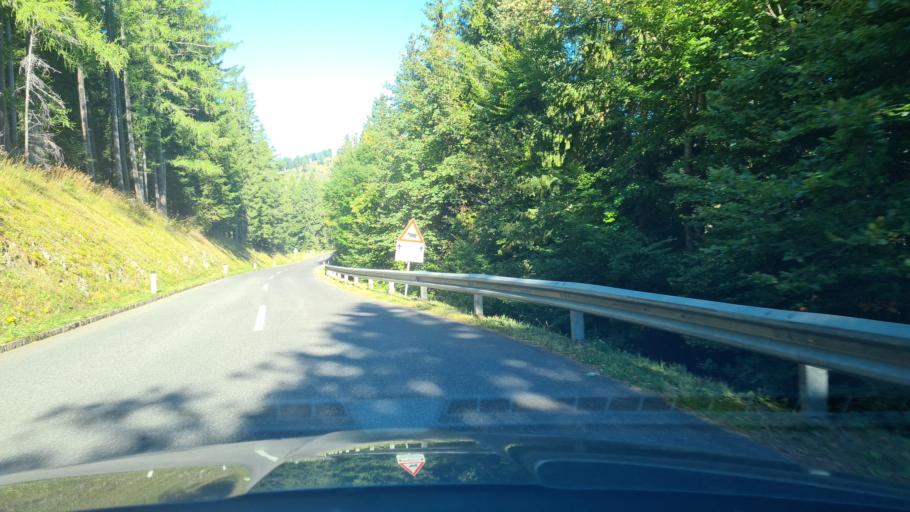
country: AT
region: Styria
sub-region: Politischer Bezirk Weiz
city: Passail
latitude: 47.3258
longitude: 15.4778
